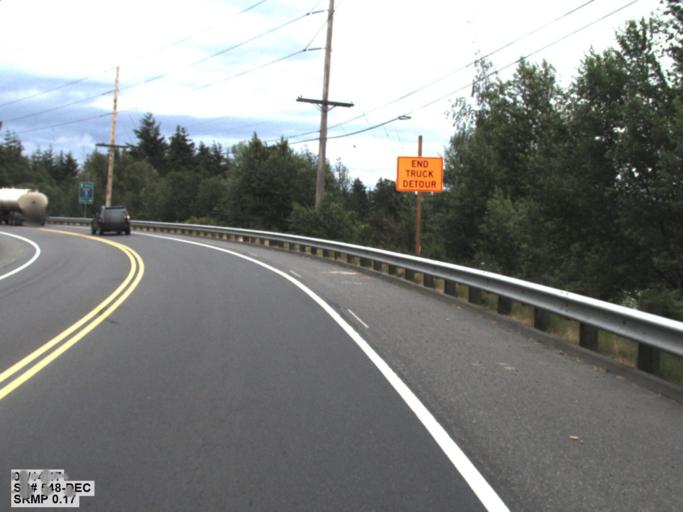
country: US
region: Washington
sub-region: Whatcom County
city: Ferndale
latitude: 48.8916
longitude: -122.6000
